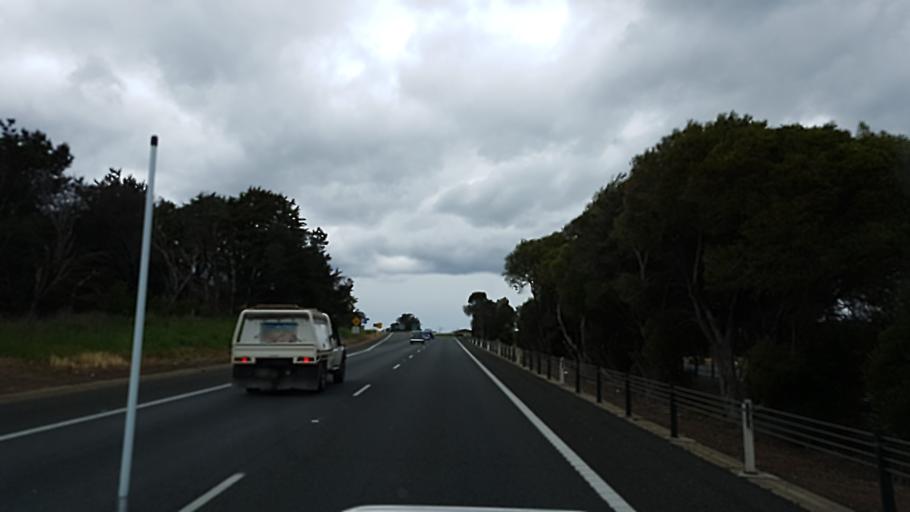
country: AU
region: Victoria
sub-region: Moorabool
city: Bacchus Marsh
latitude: -37.6096
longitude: 144.3127
